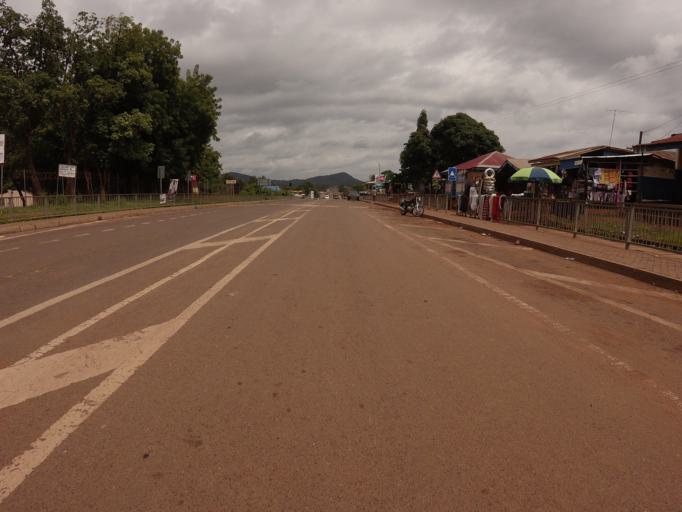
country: TG
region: Centrale
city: Sotouboua
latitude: 8.2591
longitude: 0.5220
